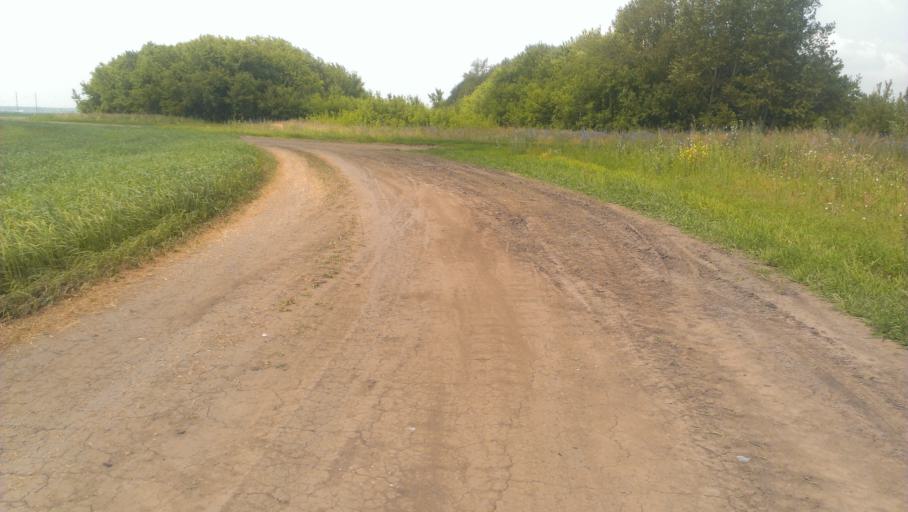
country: RU
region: Altai Krai
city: Gon'ba
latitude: 53.3837
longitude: 83.6232
